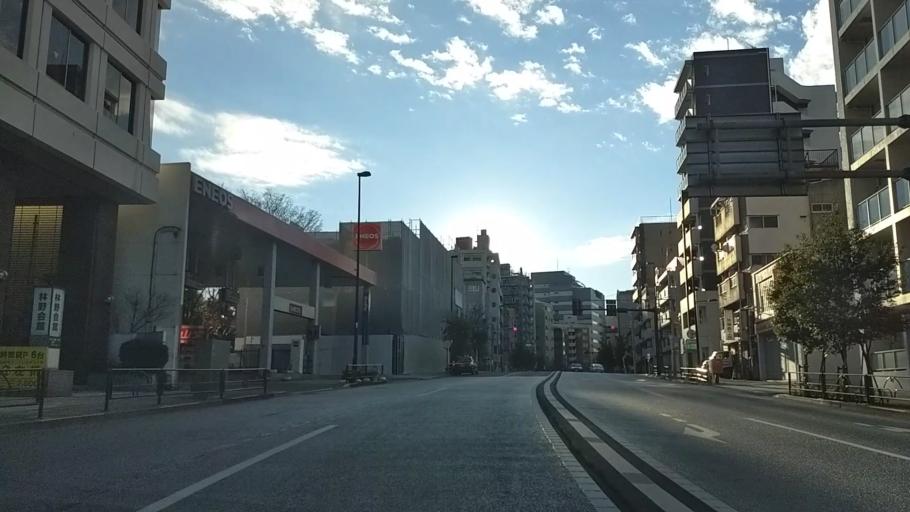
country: JP
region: Tokyo
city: Tokyo
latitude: 35.7229
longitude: 139.7365
